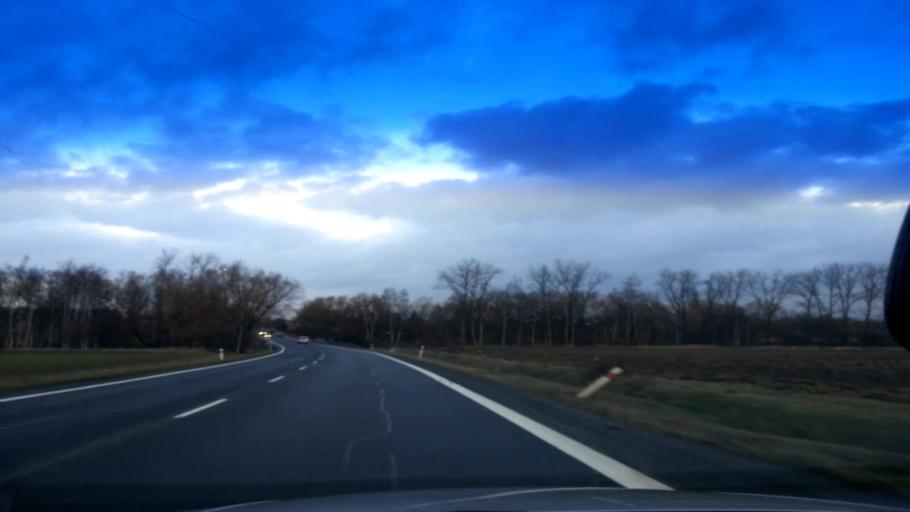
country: CZ
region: Karlovarsky
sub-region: Okres Cheb
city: Frantiskovy Lazne
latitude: 50.1091
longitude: 12.3721
